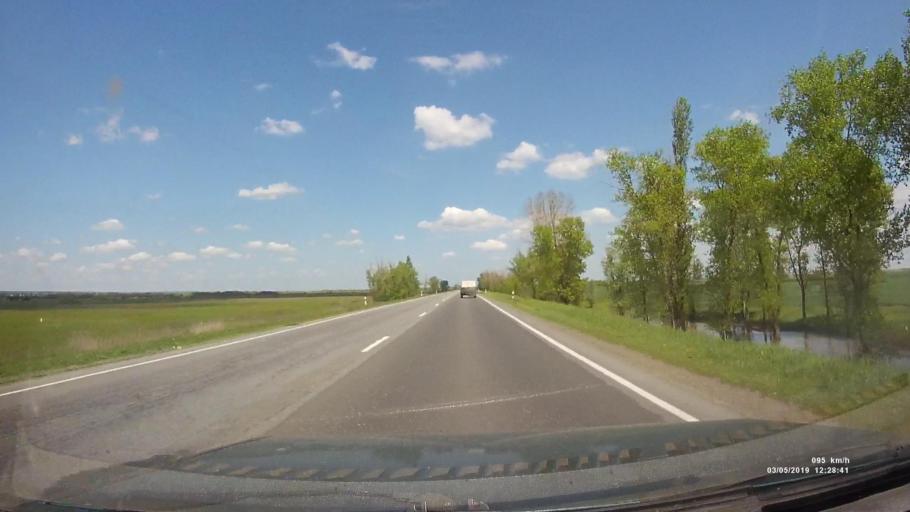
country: RU
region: Rostov
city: Semikarakorsk
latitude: 47.4771
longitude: 40.7303
